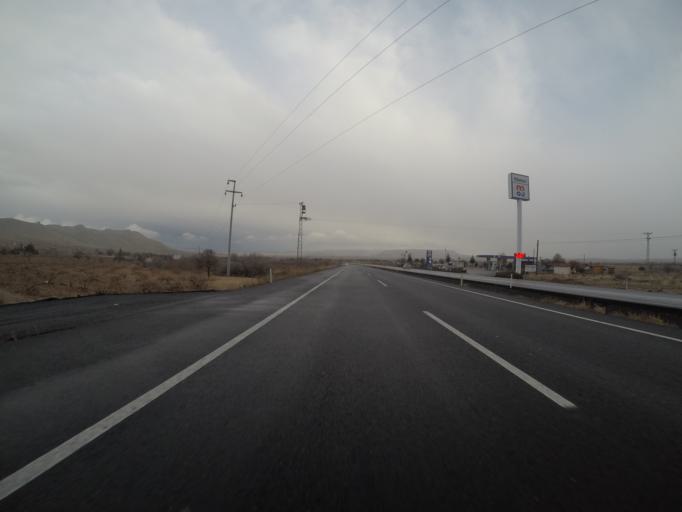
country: TR
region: Nevsehir
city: Goereme
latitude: 38.6783
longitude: 34.7819
